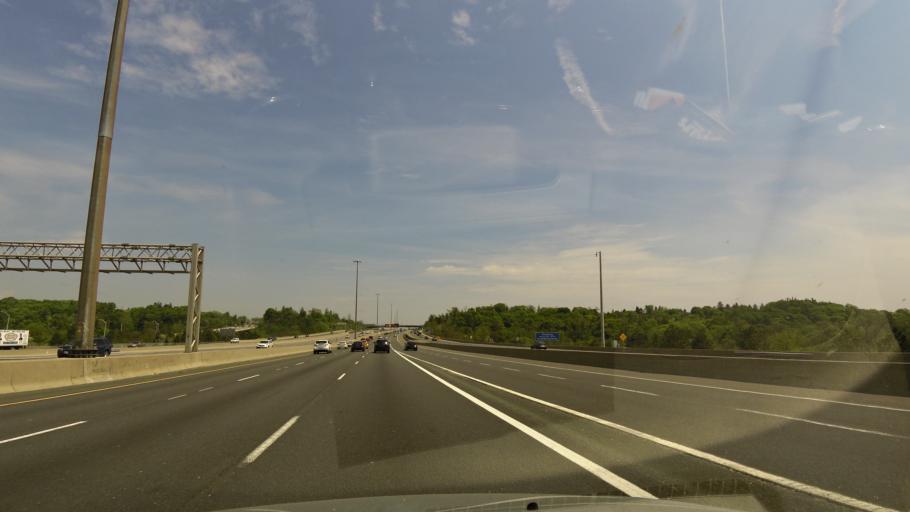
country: CA
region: Ontario
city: Pickering
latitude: 43.8026
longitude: -79.1371
